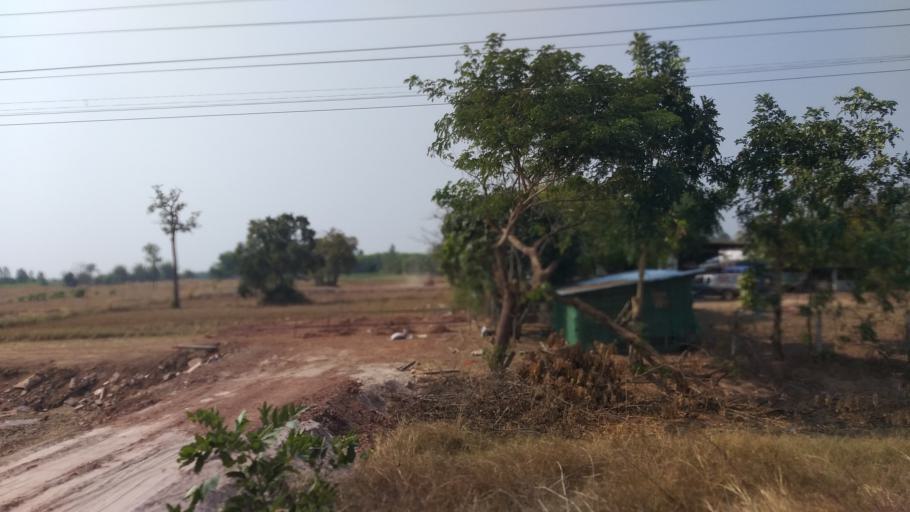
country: TH
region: Changwat Udon Thani
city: Nong Han
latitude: 17.3819
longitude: 103.1855
